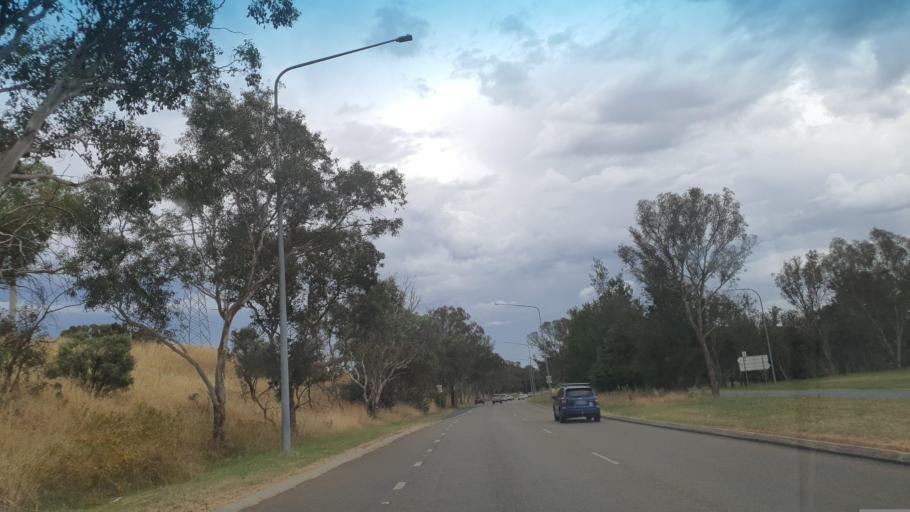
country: AU
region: Australian Capital Territory
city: Macquarie
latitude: -35.2172
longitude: 149.0427
